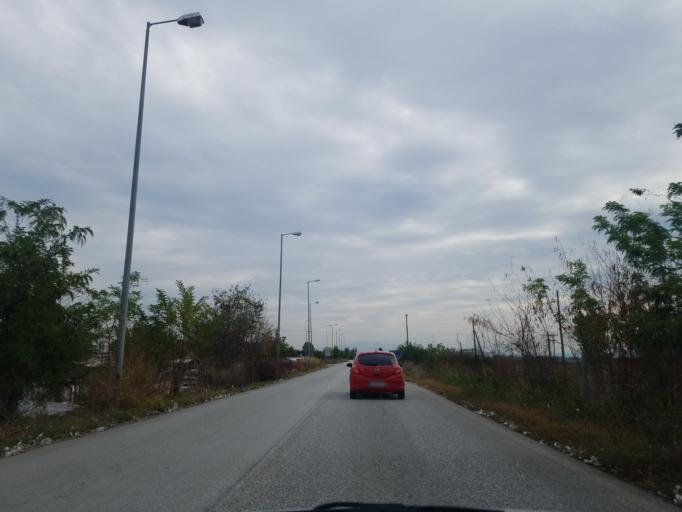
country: GR
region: Thessaly
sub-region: Nomos Kardhitsas
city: Sofades
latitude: 39.3262
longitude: 22.0963
